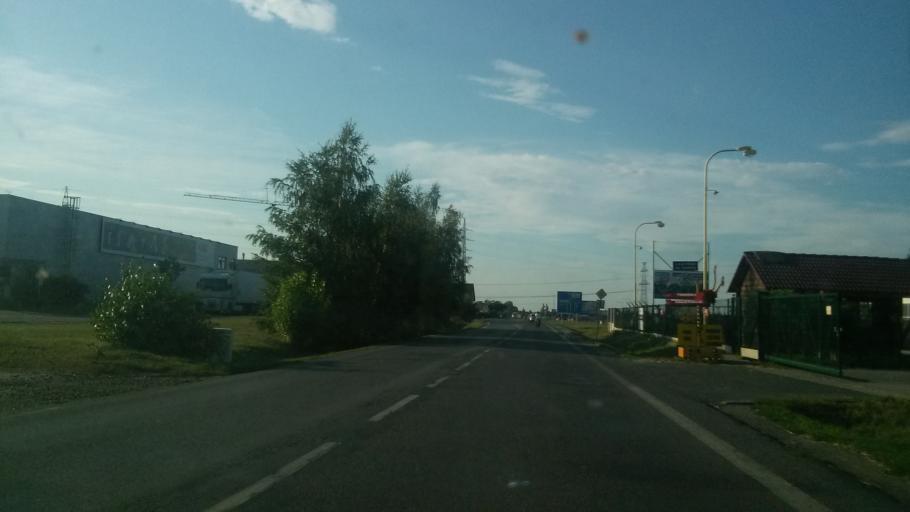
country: CZ
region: Central Bohemia
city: Vestec
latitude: 49.9883
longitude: 14.4922
